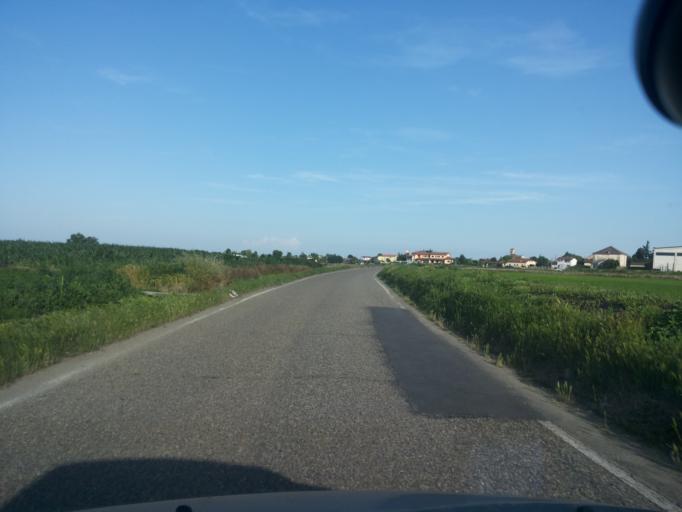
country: IT
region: Piedmont
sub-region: Provincia di Vercelli
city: Pezzana
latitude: 45.2670
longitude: 8.4748
